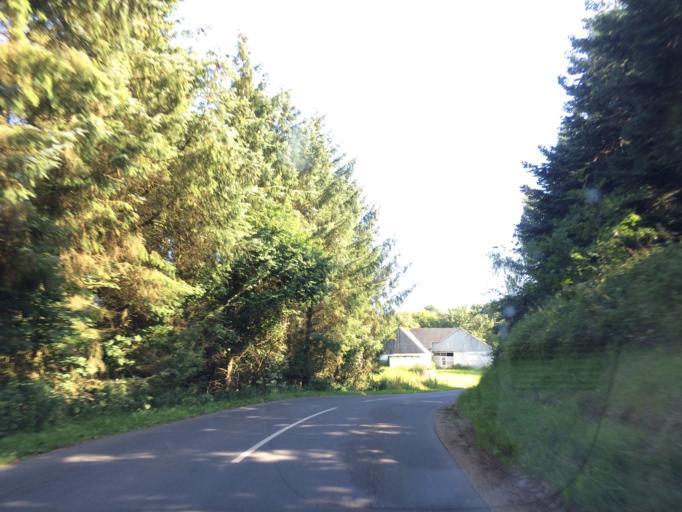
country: DK
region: Central Jutland
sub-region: Syddjurs Kommune
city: Ebeltoft
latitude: 56.2421
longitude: 10.6157
